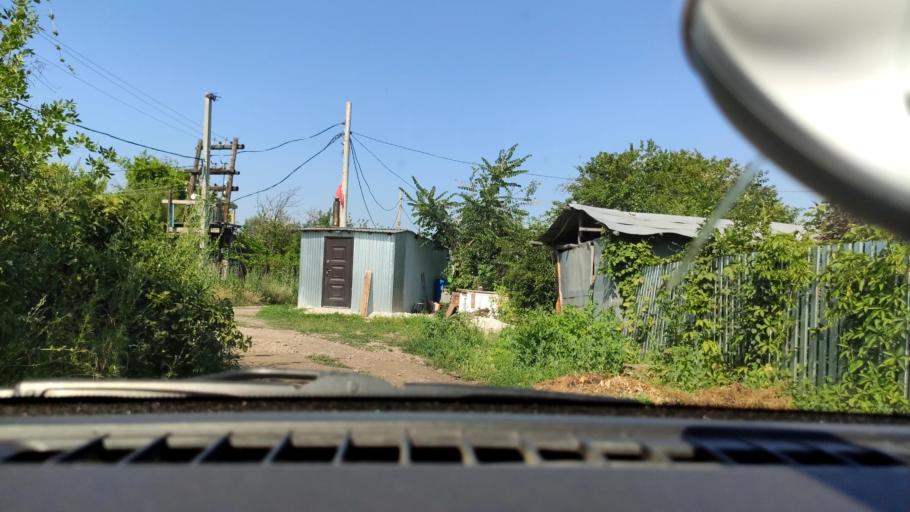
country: RU
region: Samara
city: Petra-Dubrava
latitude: 53.2690
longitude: 50.2971
